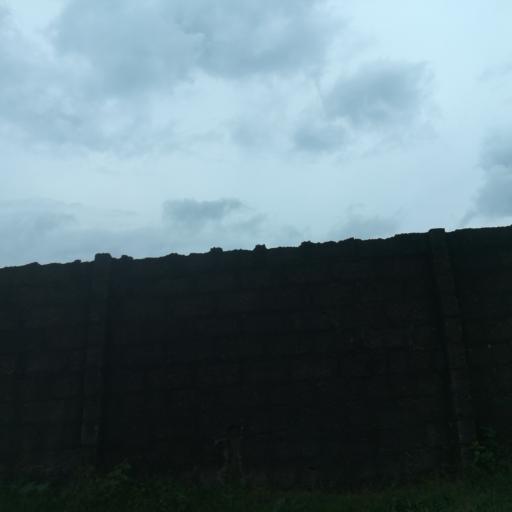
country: NG
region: Rivers
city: Port Harcourt
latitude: 4.8224
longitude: 7.0392
